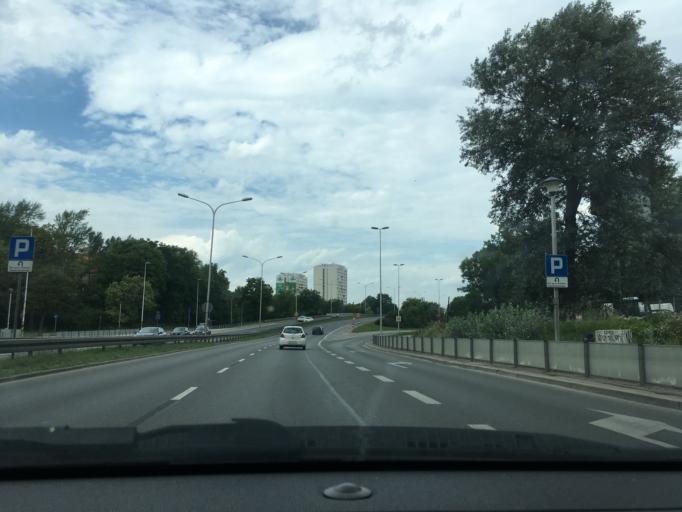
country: PL
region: Masovian Voivodeship
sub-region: Warszawa
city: Zoliborz
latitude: 52.2693
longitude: 20.9993
